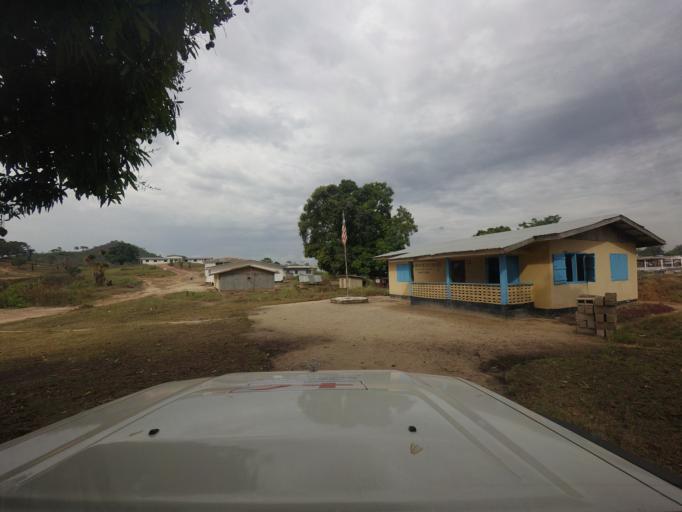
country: SL
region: Eastern Province
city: Buedu
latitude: 8.2816
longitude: -10.0868
